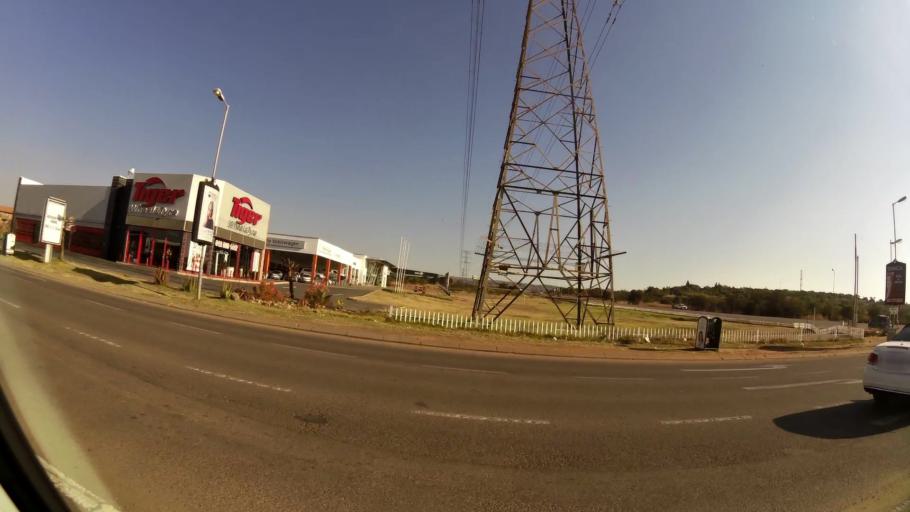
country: ZA
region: Gauteng
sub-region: City of Tshwane Metropolitan Municipality
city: Pretoria
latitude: -25.7671
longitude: 28.3574
